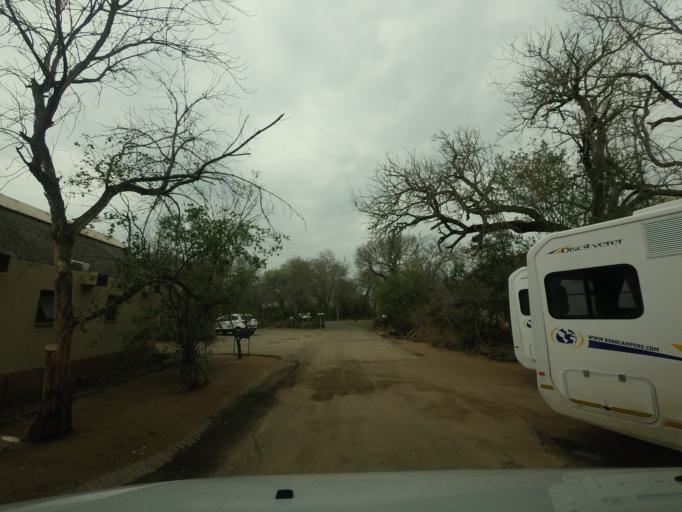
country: ZA
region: Limpopo
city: Thulamahashi
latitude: -24.4754
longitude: 31.3904
